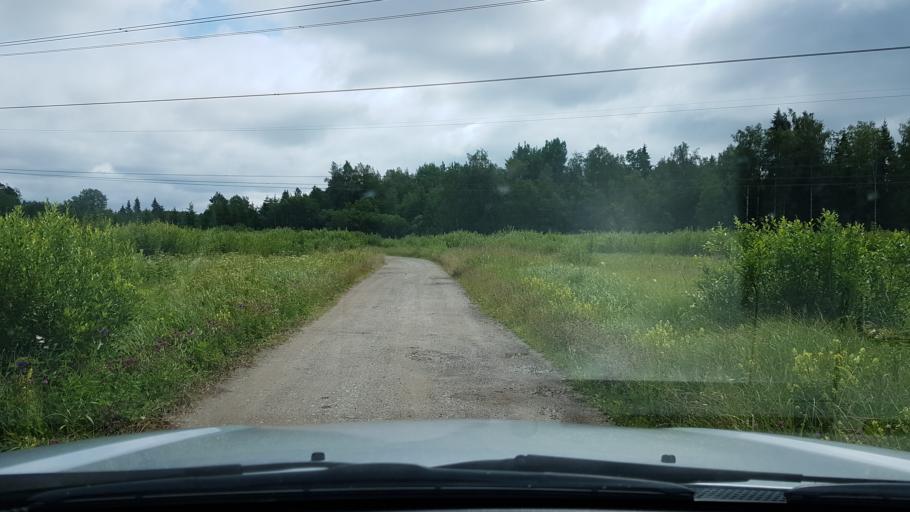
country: EE
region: Ida-Virumaa
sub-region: Narva-Joesuu linn
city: Narva-Joesuu
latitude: 59.3651
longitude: 28.0740
